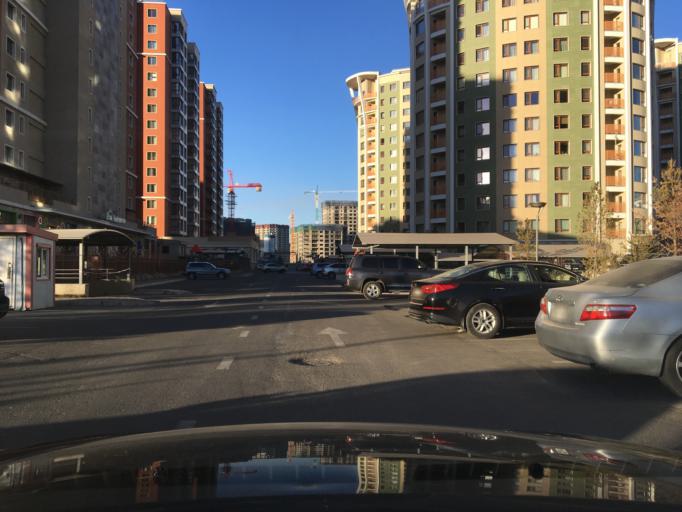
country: MN
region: Ulaanbaatar
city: Ulaanbaatar
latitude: 47.8898
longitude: 106.9260
